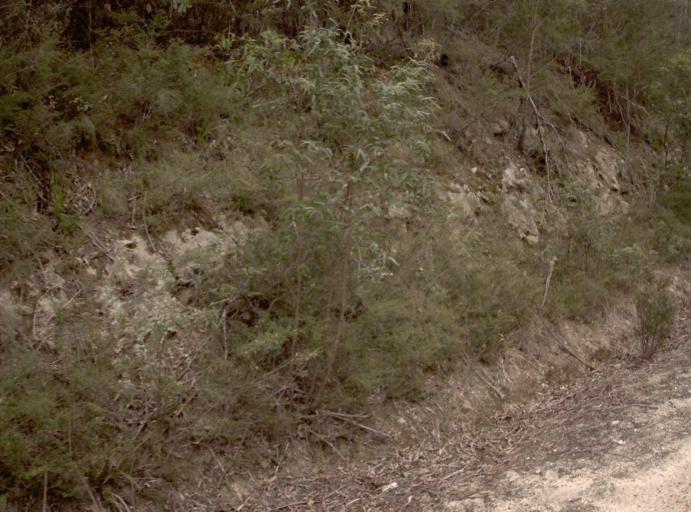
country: AU
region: New South Wales
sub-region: Bombala
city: Bombala
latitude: -37.3412
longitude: 149.2063
